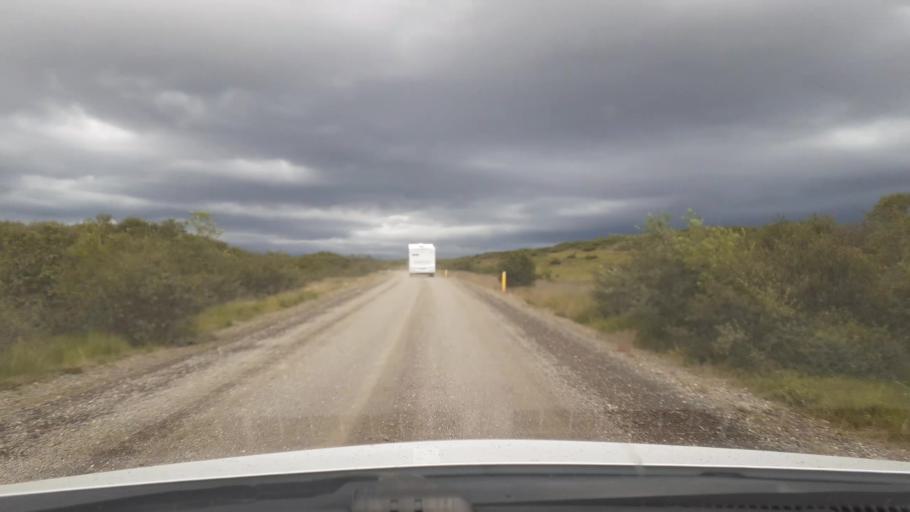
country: IS
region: West
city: Borgarnes
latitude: 64.5487
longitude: -21.6196
